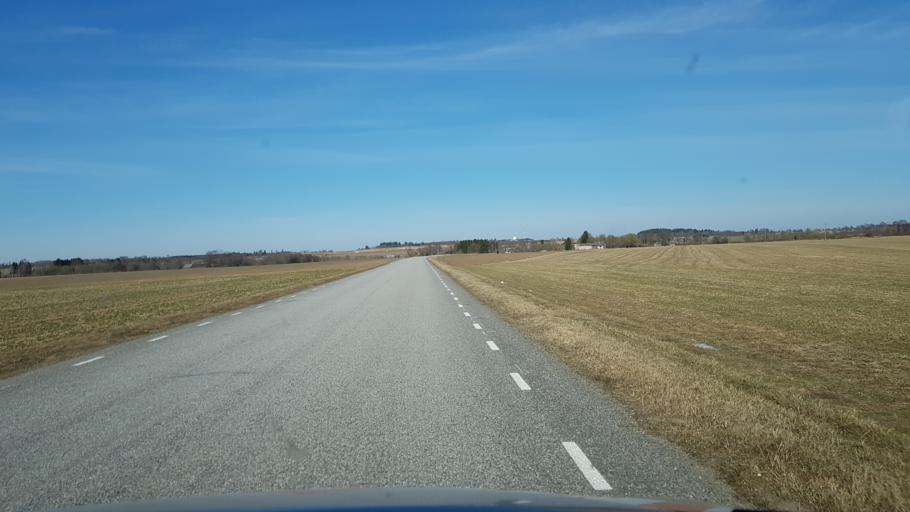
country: EE
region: Laeaene-Virumaa
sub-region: Vaeike-Maarja vald
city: Vaike-Maarja
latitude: 59.0611
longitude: 26.4703
